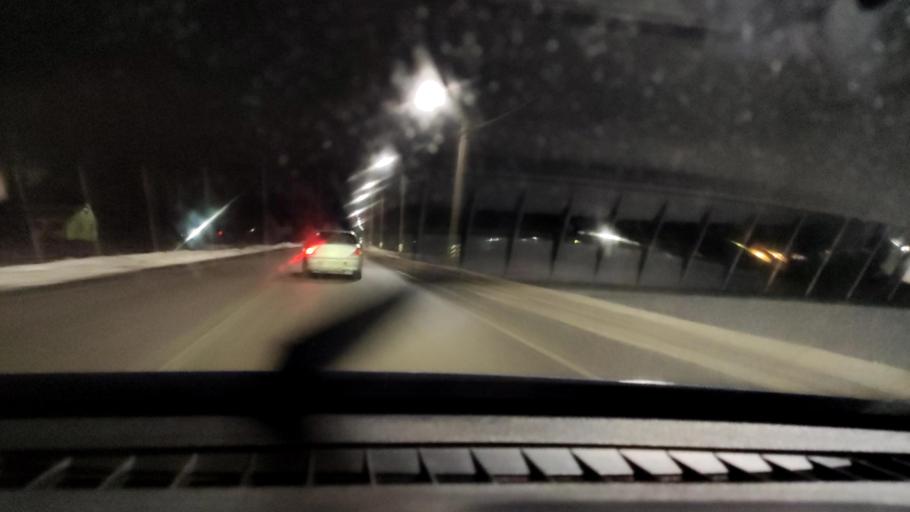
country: RU
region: Voronezj
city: Novaya Usman'
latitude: 51.6636
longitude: 39.4467
